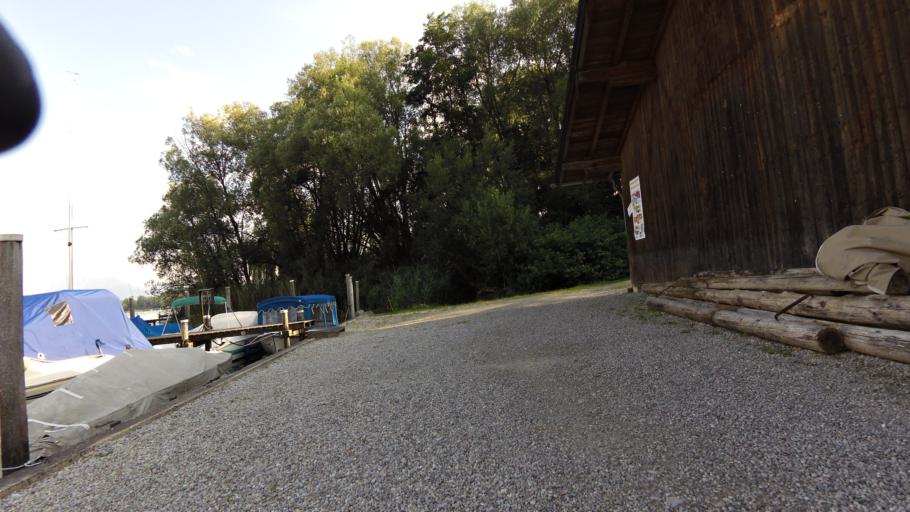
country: DE
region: Bavaria
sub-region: Upper Bavaria
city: Gstadt am Chiemsee
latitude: 47.8789
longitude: 12.3897
